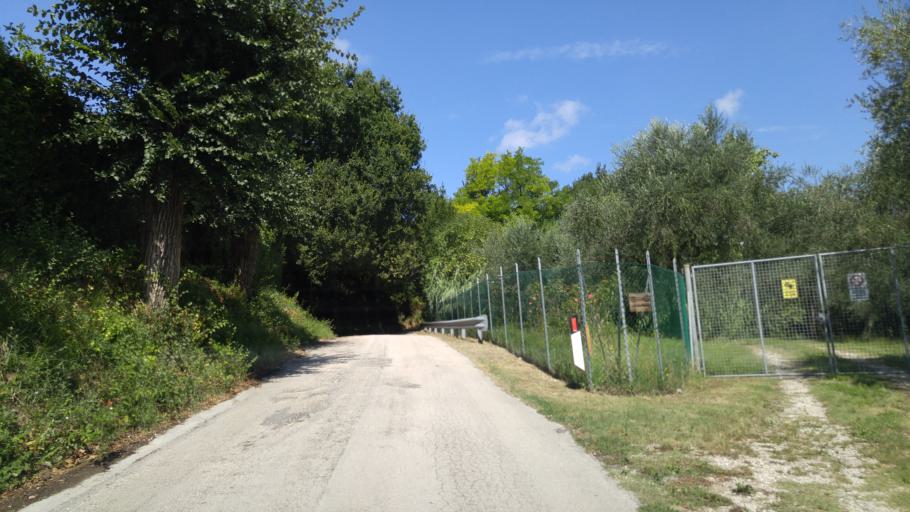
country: IT
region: The Marches
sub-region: Provincia di Pesaro e Urbino
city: Fenile
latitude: 43.8256
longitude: 12.9721
